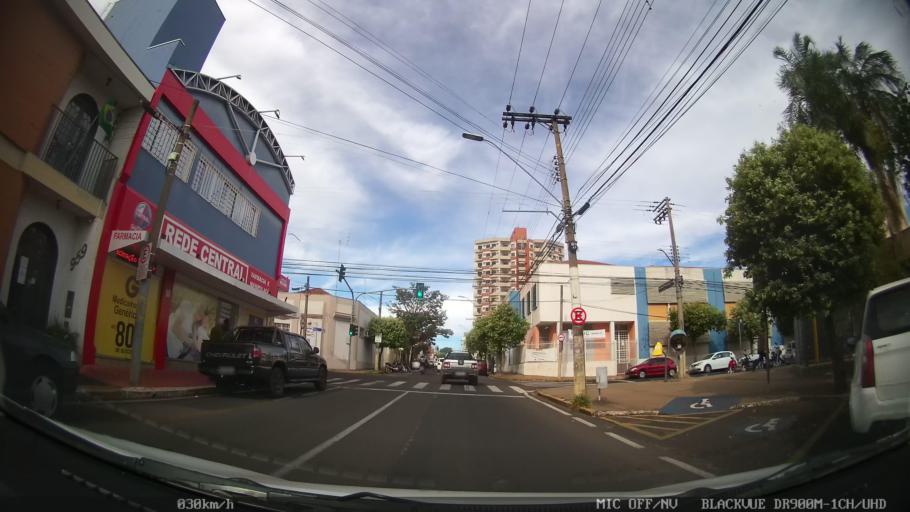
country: BR
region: Sao Paulo
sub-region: Catanduva
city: Catanduva
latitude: -21.1391
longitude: -48.9746
